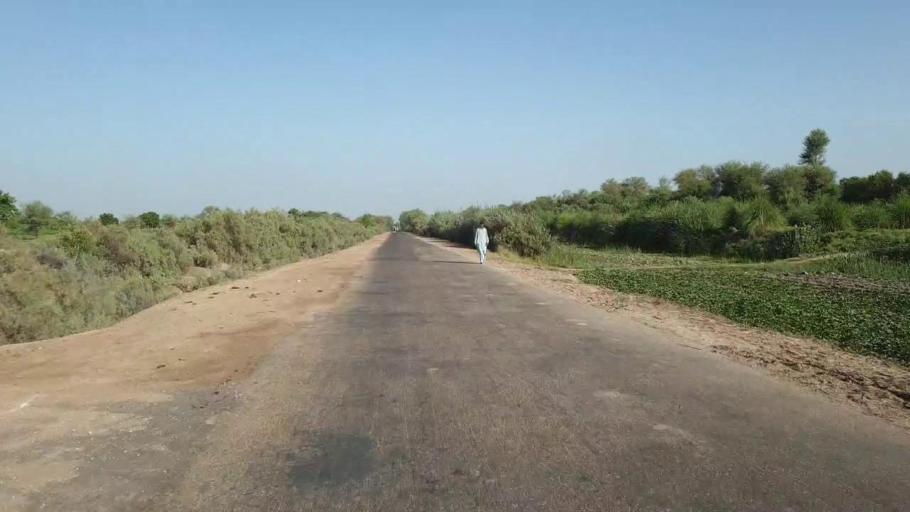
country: PK
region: Sindh
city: Nawabshah
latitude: 26.3829
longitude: 68.4565
